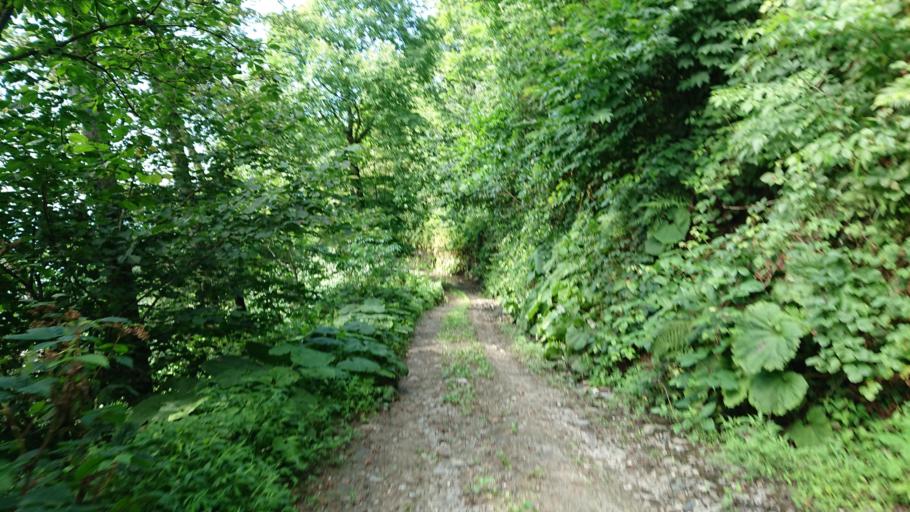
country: TR
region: Rize
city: Rize
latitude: 40.9758
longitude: 40.4987
